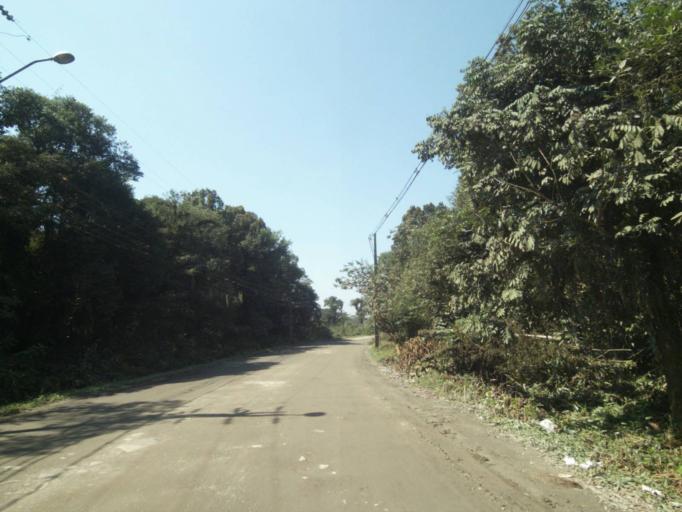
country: BR
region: Parana
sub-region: Paranagua
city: Paranagua
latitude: -25.5500
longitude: -48.5850
